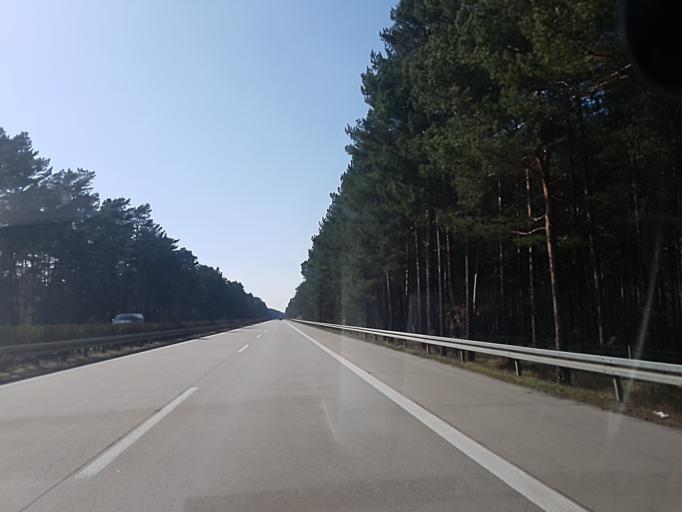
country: DE
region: Brandenburg
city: Forst
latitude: 51.7093
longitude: 14.5344
